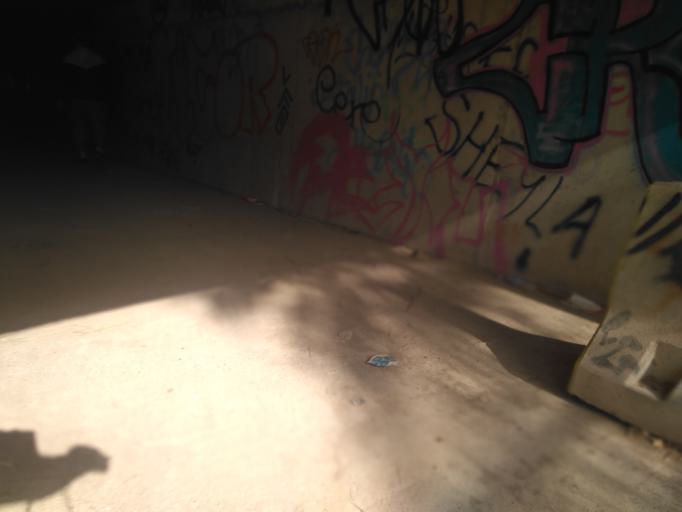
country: ES
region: Valencia
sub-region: Provincia de Valencia
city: Alboraya
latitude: 39.5017
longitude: -0.3255
